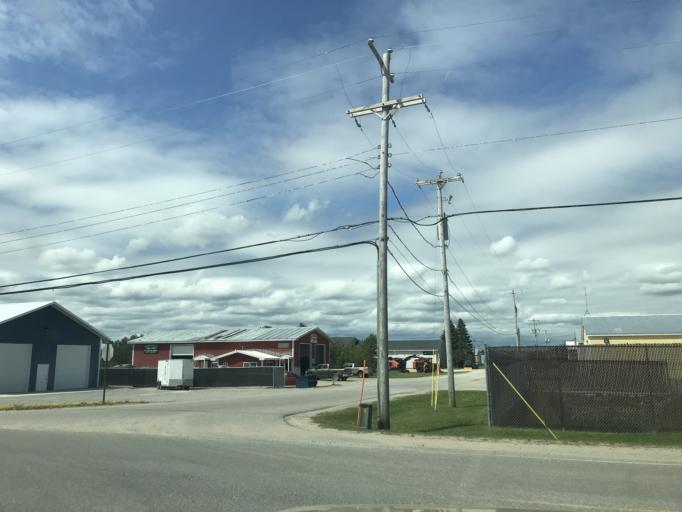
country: US
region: Michigan
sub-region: Otsego County
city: Gaylord
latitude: 45.0298
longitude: -84.6941
